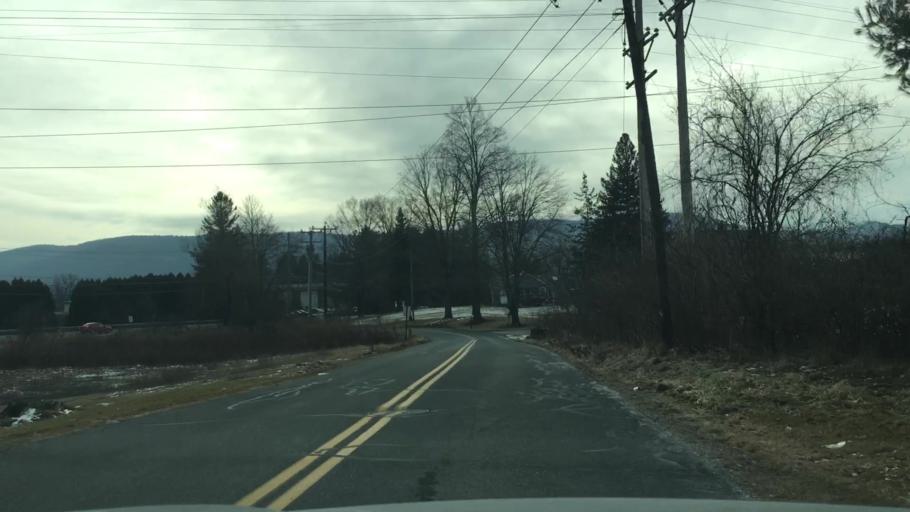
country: US
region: Massachusetts
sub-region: Berkshire County
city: Lee
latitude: 42.2870
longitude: -73.2458
